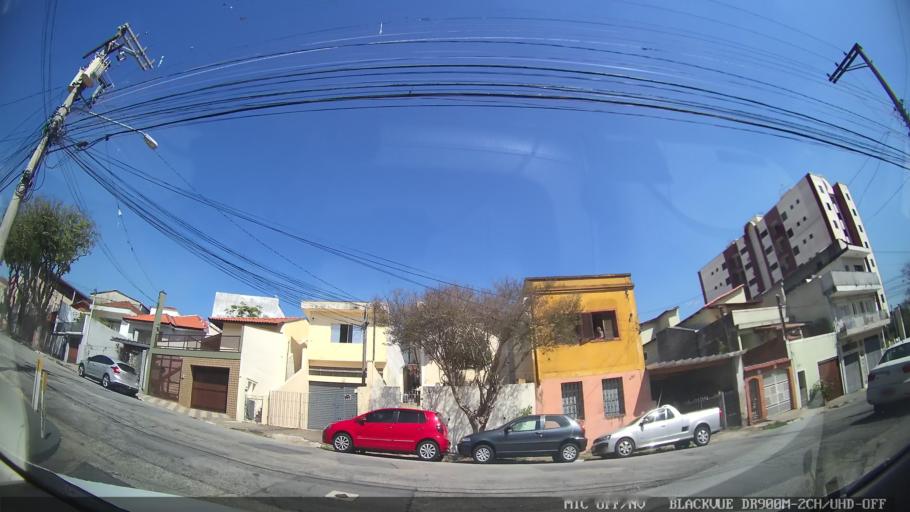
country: BR
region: Sao Paulo
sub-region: Sao Paulo
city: Sao Paulo
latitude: -23.5070
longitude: -46.6574
